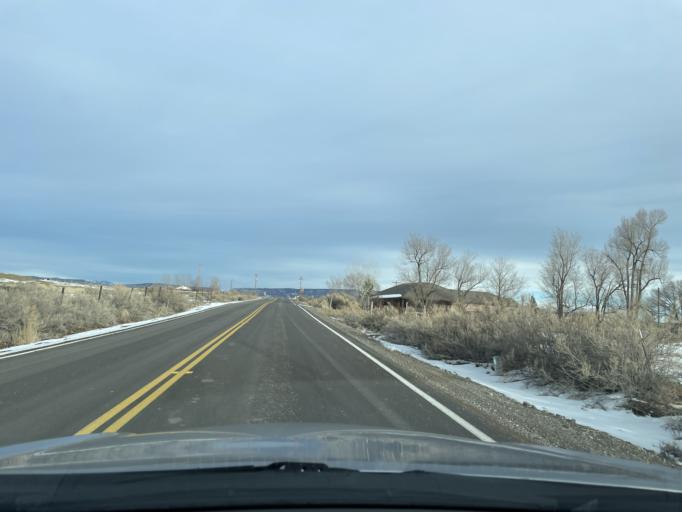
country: US
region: Colorado
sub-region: Montrose County
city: Olathe
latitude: 38.6497
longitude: -107.9925
